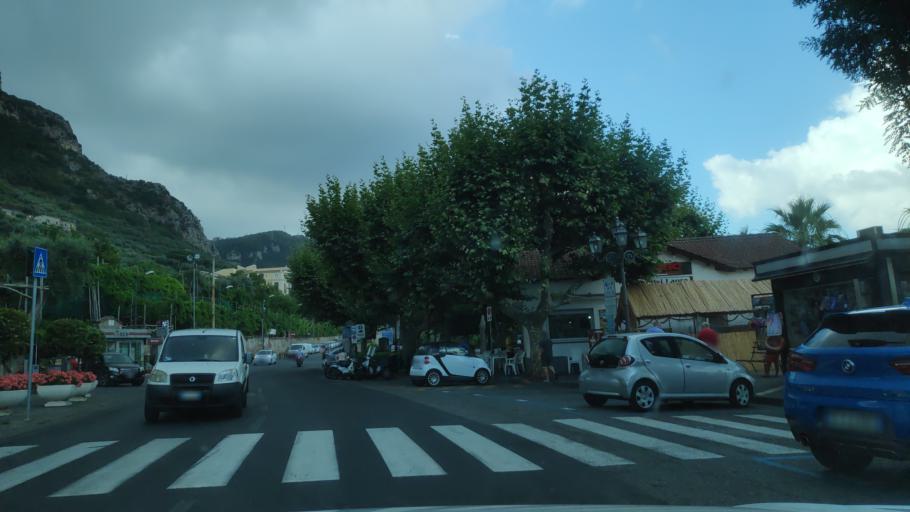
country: IT
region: Campania
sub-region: Provincia di Napoli
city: Meta
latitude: 40.6418
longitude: 14.4177
